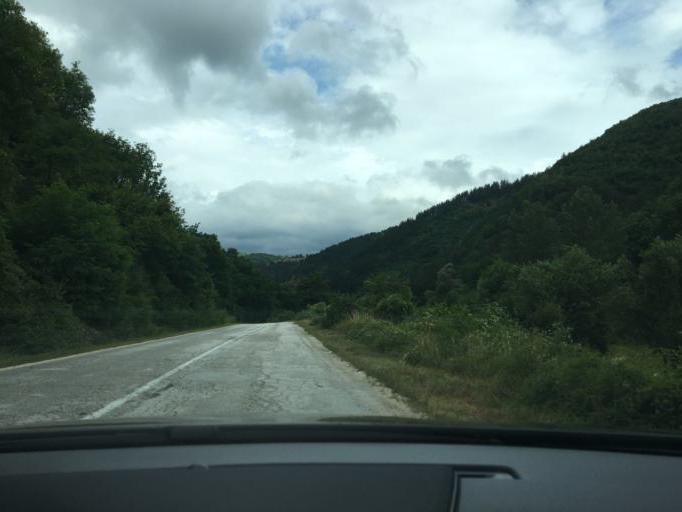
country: MK
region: Kriva Palanka
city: Kriva Palanka
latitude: 42.2266
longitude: 22.3853
